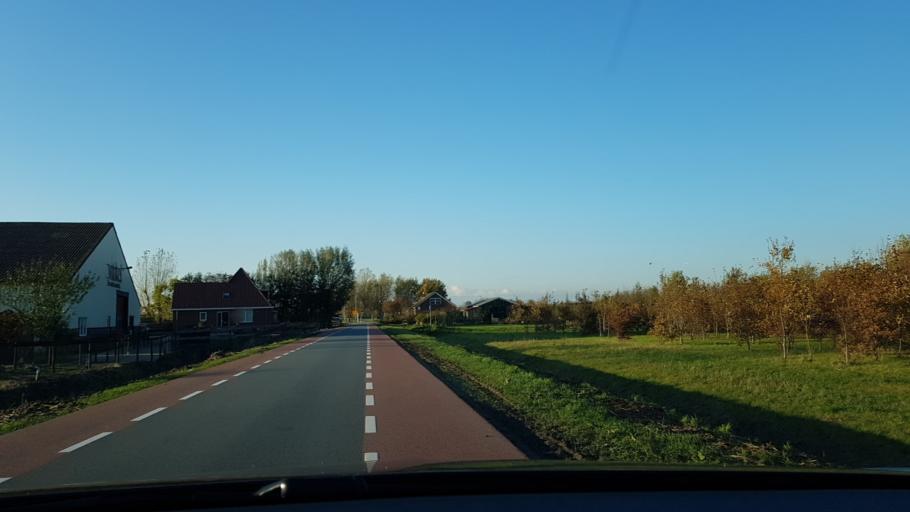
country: NL
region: North Holland
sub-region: Gemeente Beverwijk
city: Beverwijk
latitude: 52.4726
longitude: 4.6874
